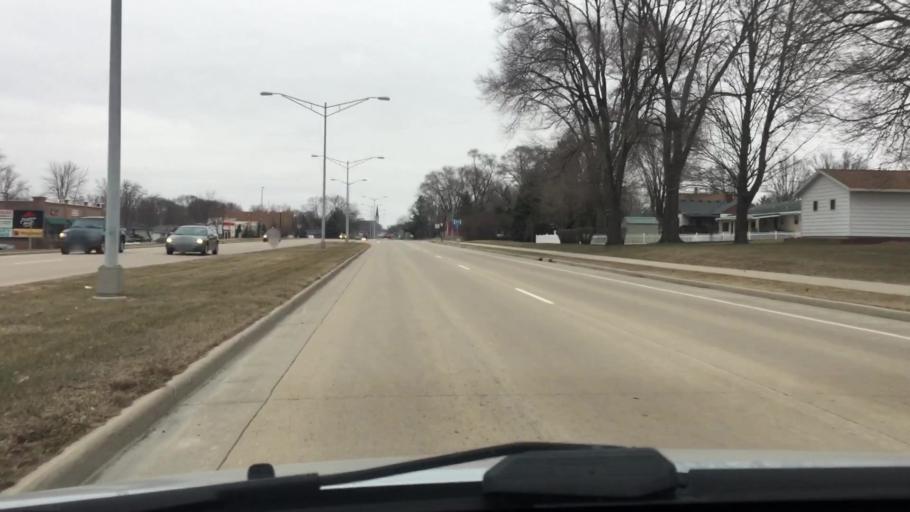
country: US
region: Wisconsin
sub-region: Jefferson County
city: Watertown
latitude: 43.1776
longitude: -88.7313
